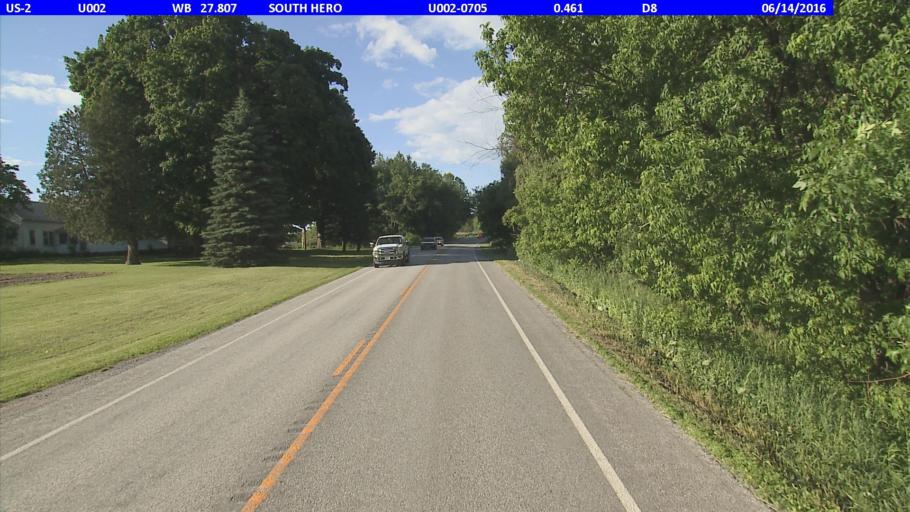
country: US
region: New York
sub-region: Clinton County
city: Cumberland Head
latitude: 44.6742
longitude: -73.3200
